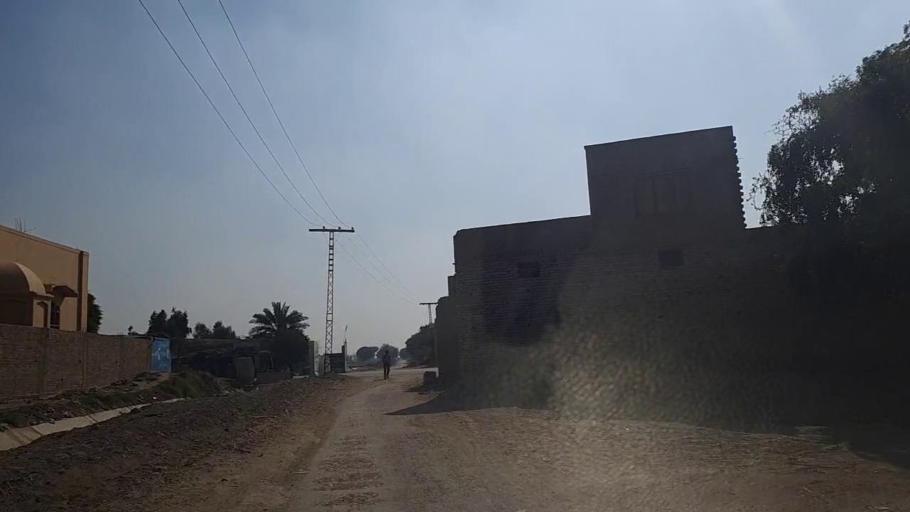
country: PK
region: Sindh
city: Shahpur Chakar
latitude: 26.1887
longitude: 68.5835
